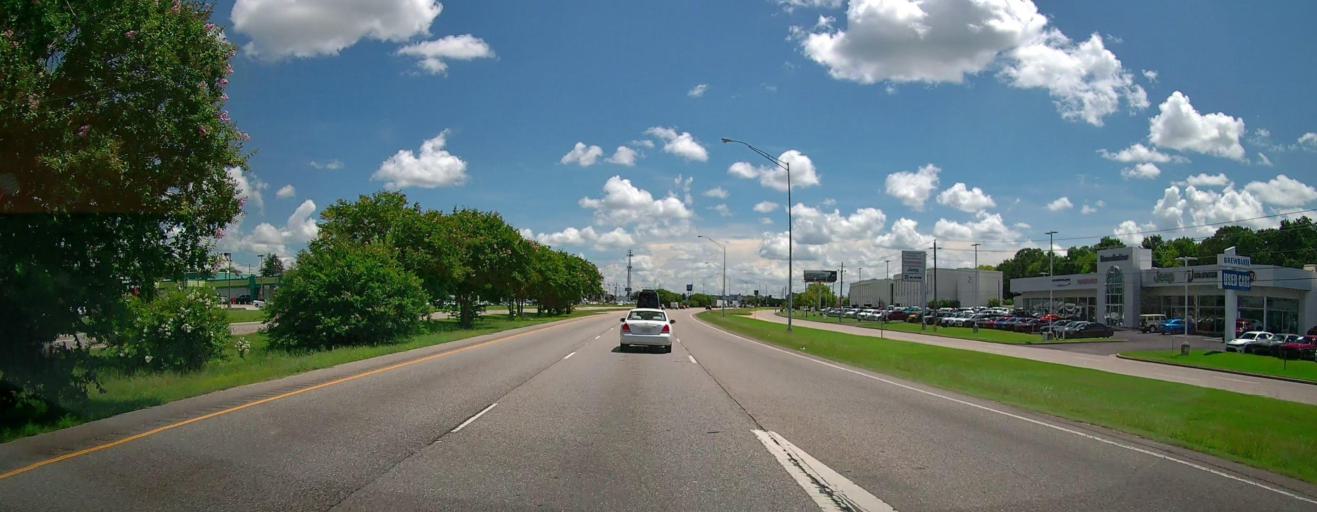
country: US
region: Alabama
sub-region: Montgomery County
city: Montgomery
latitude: 32.3755
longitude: -86.2095
